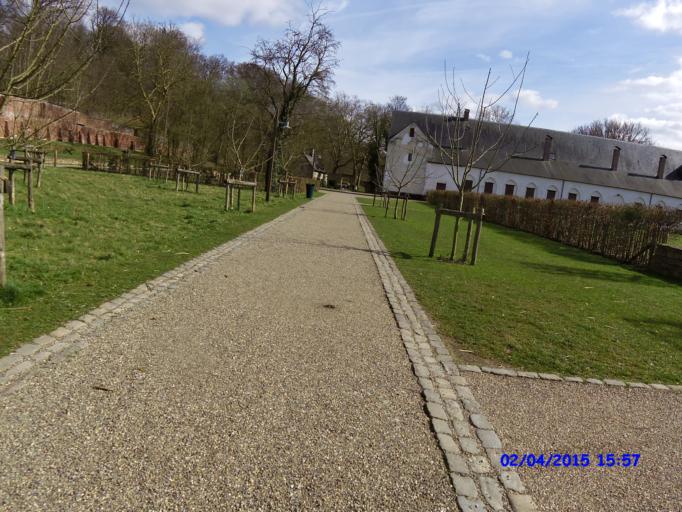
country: BE
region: Flanders
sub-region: Provincie Vlaams-Brabant
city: Hoeilaart
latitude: 50.8138
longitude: 4.4441
